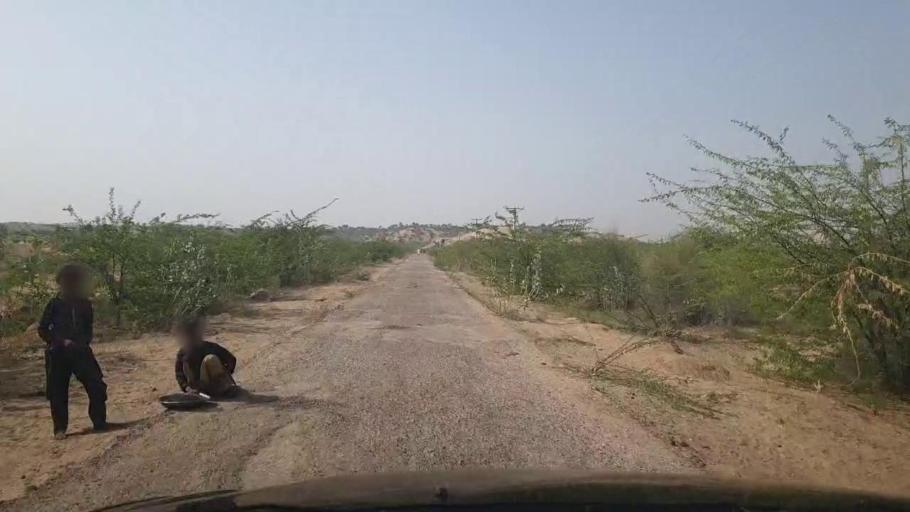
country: PK
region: Sindh
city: Islamkot
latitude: 25.0062
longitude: 70.2110
